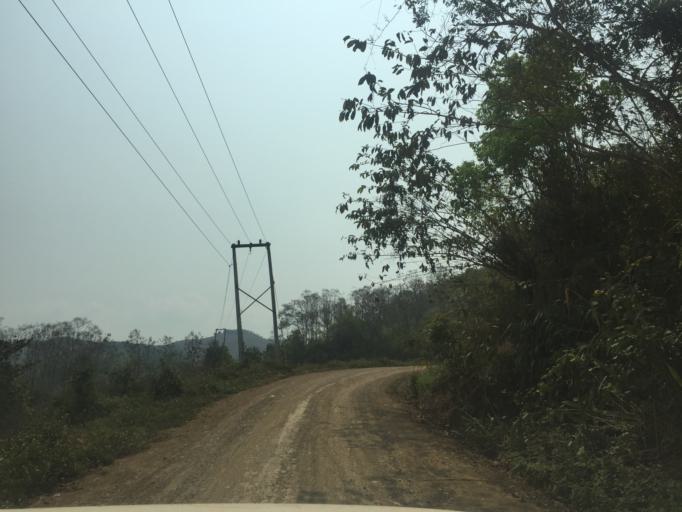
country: LA
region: Loungnamtha
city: Muang Nale
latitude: 20.3018
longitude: 101.6586
